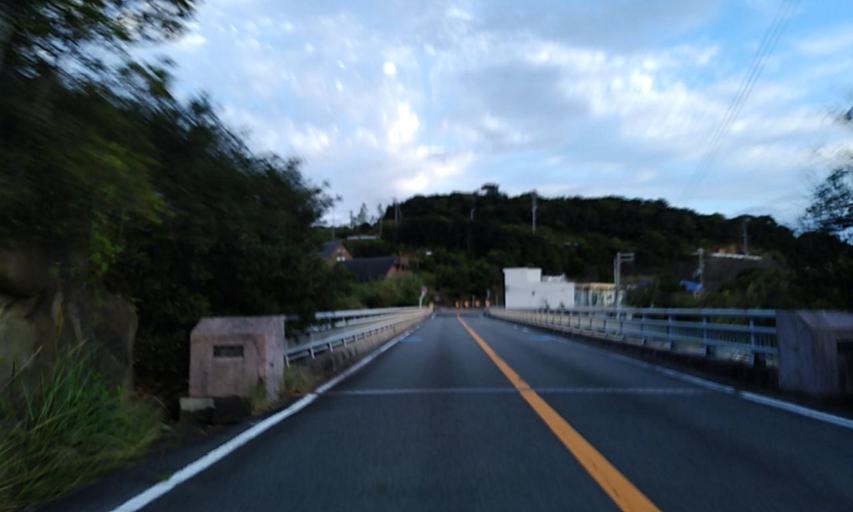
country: JP
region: Wakayama
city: Tanabe
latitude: 33.6647
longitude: 135.3401
